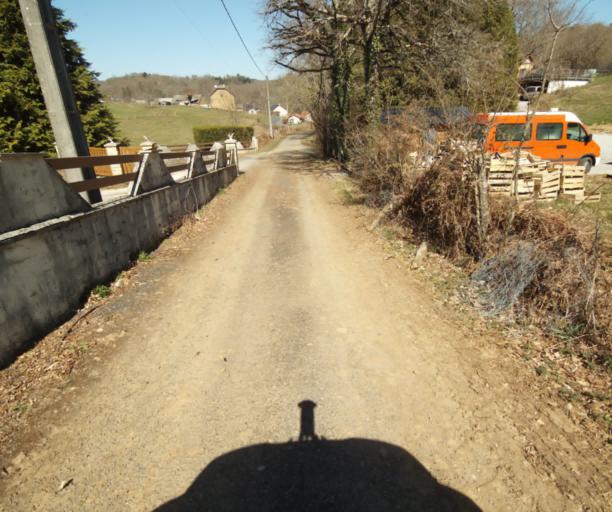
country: FR
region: Limousin
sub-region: Departement de la Correze
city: Saint-Clement
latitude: 45.3137
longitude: 1.7052
